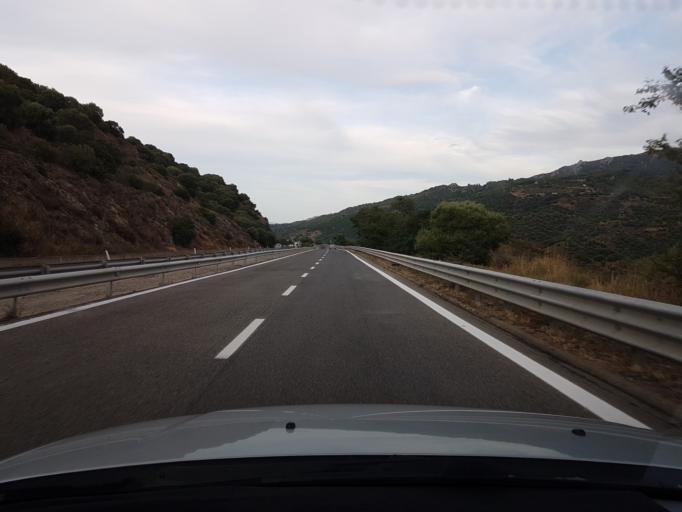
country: IT
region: Sardinia
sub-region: Provincia di Nuoro
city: Nuoro
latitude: 40.3442
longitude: 9.3196
